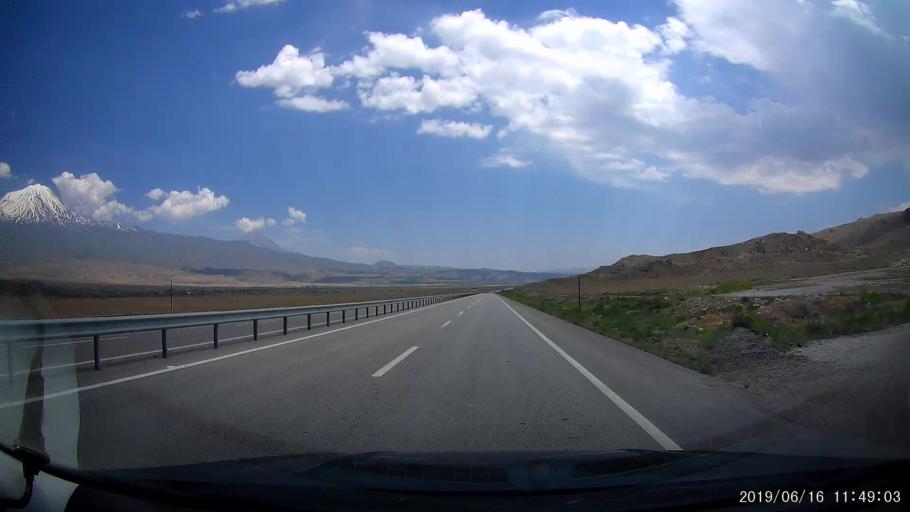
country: TR
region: Agri
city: Dogubayazit
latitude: 39.5577
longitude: 44.1560
